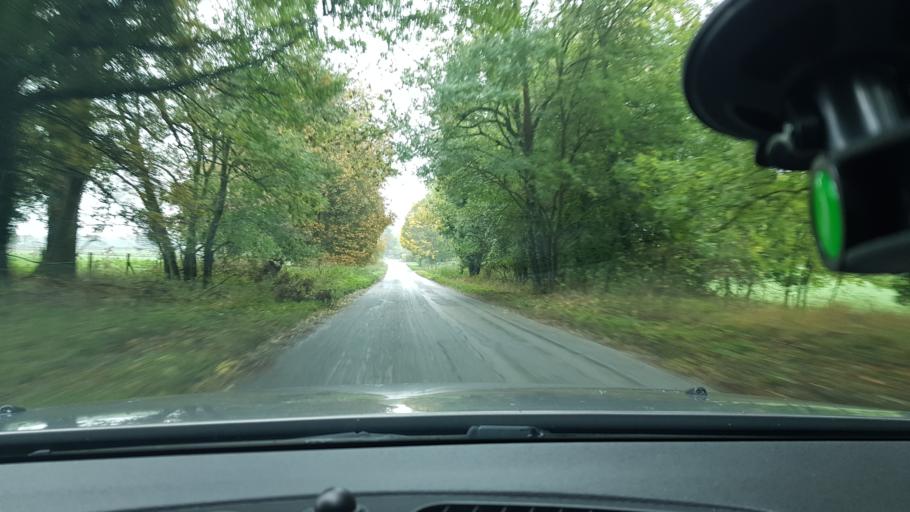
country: GB
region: England
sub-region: Wiltshire
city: Great Bedwyn
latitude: 51.3882
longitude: -1.6444
